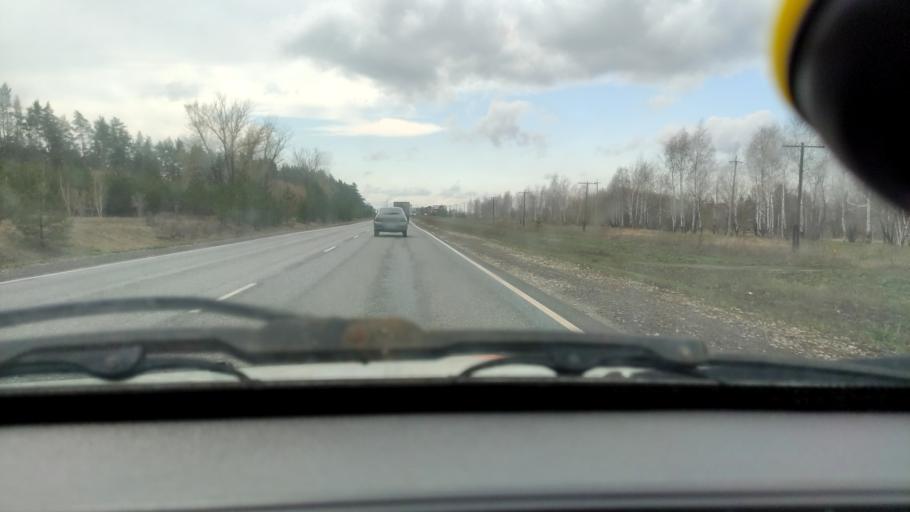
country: RU
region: Samara
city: Povolzhskiy
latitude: 53.5962
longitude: 49.5875
